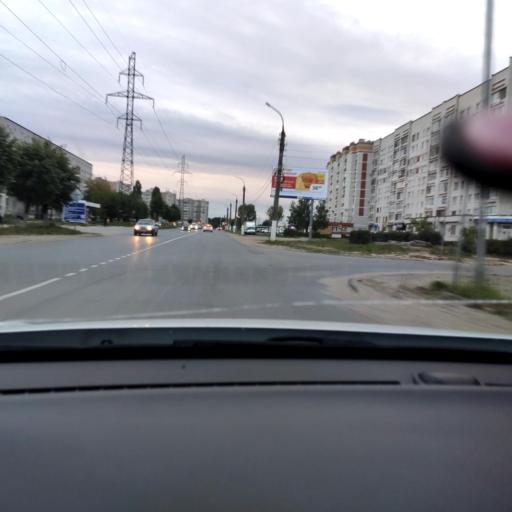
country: RU
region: Mariy-El
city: Volzhsk
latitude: 55.8665
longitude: 48.3548
